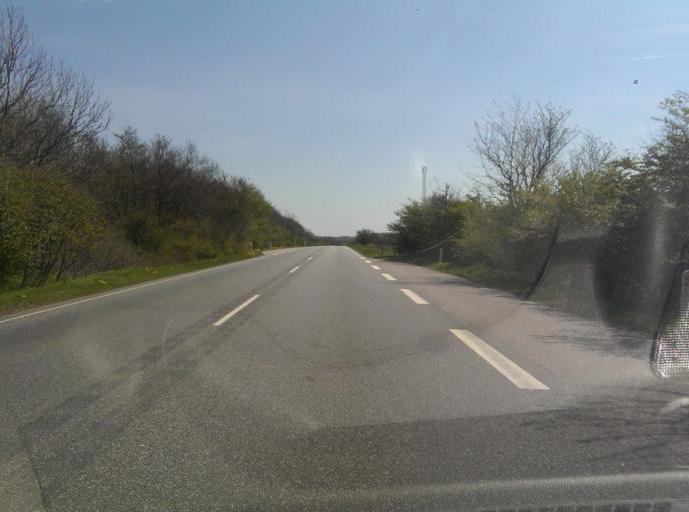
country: DK
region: South Denmark
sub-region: Esbjerg Kommune
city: Bramming
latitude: 55.4226
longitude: 8.6930
